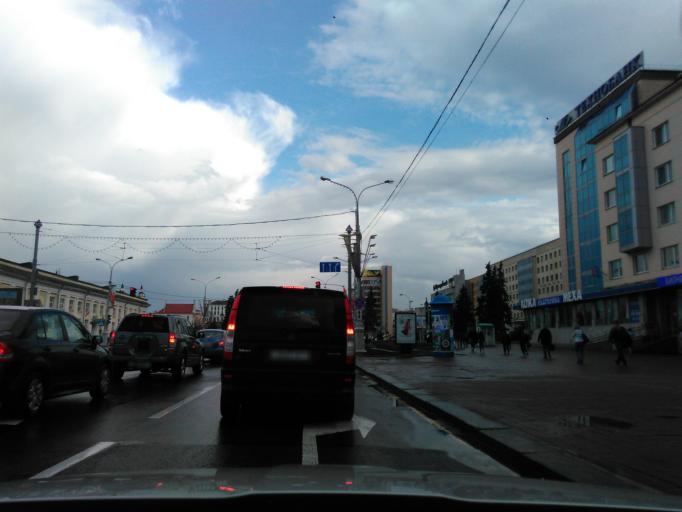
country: BY
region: Minsk
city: Minsk
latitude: 53.9077
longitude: 27.5509
